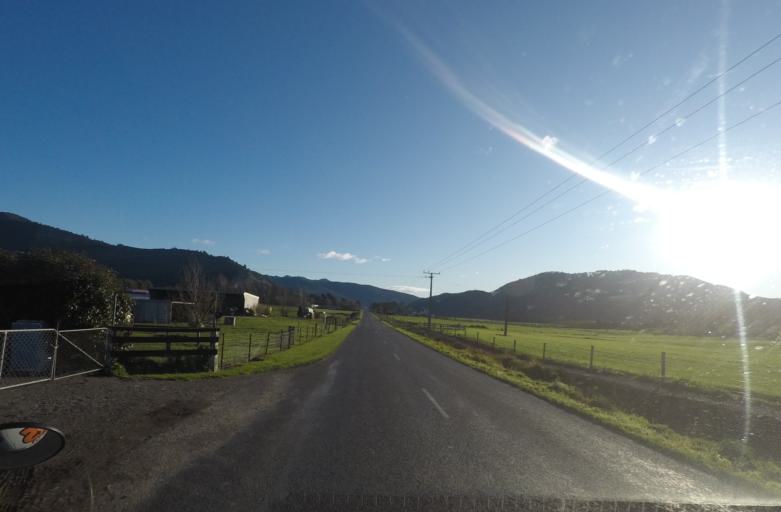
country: NZ
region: Marlborough
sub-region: Marlborough District
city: Picton
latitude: -41.2896
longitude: 173.8735
